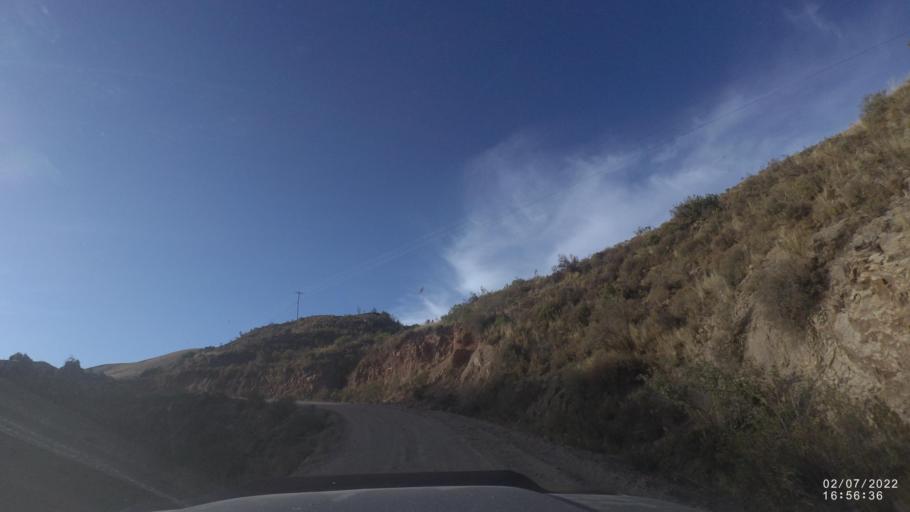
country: BO
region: Cochabamba
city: Irpa Irpa
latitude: -17.9547
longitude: -66.5439
